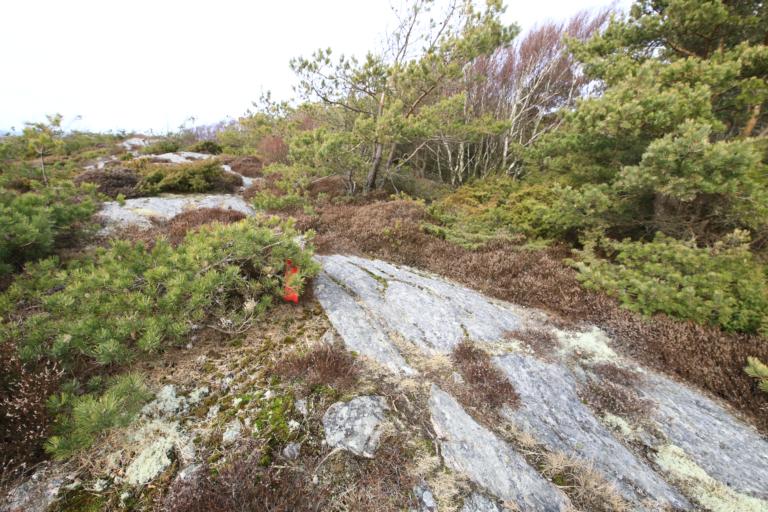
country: SE
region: Halland
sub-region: Kungsbacka Kommun
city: Frillesas
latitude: 57.2314
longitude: 12.1033
